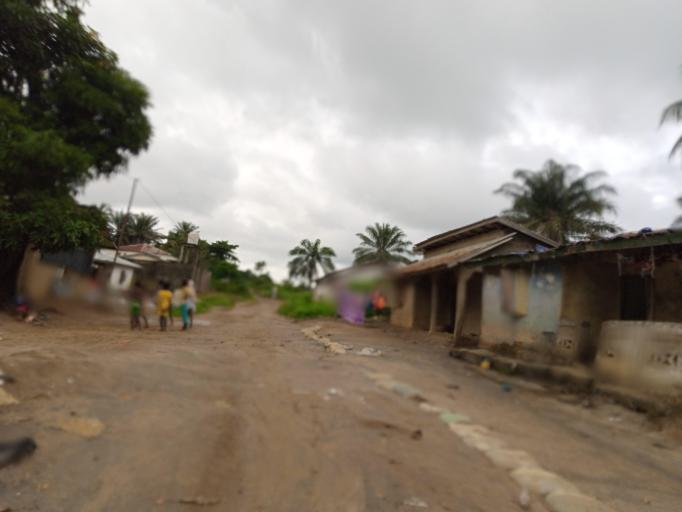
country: SL
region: Northern Province
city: Masoyila
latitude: 8.5930
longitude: -13.2017
